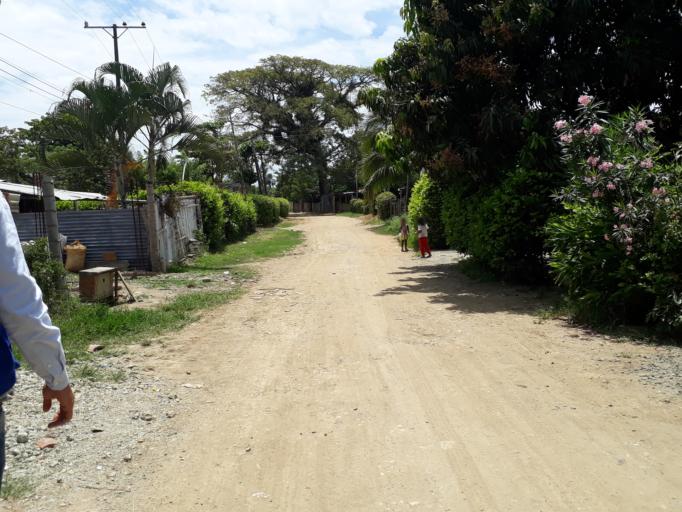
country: CO
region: Valle del Cauca
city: Cali
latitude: 3.3615
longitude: -76.4826
